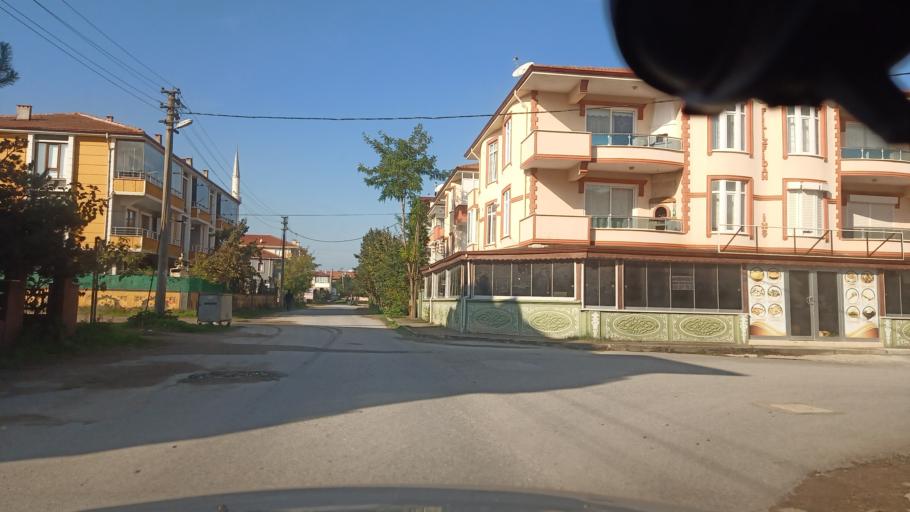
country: TR
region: Sakarya
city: Karasu
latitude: 41.0903
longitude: 30.7344
